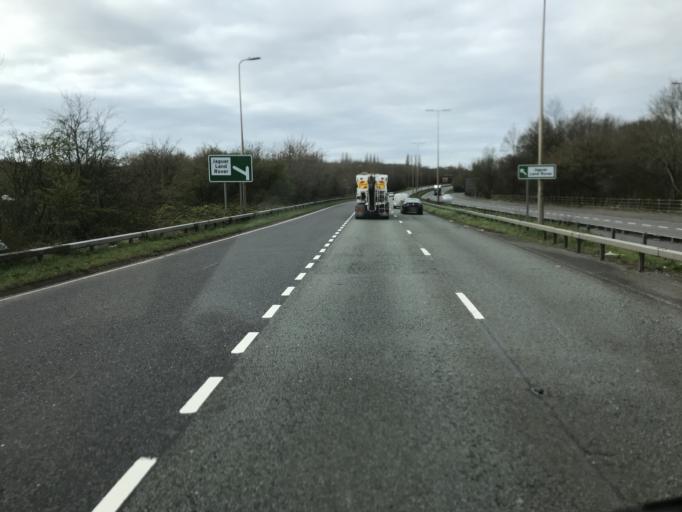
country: GB
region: England
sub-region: Borough of Halton
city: Hale
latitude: 53.3517
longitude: -2.8144
